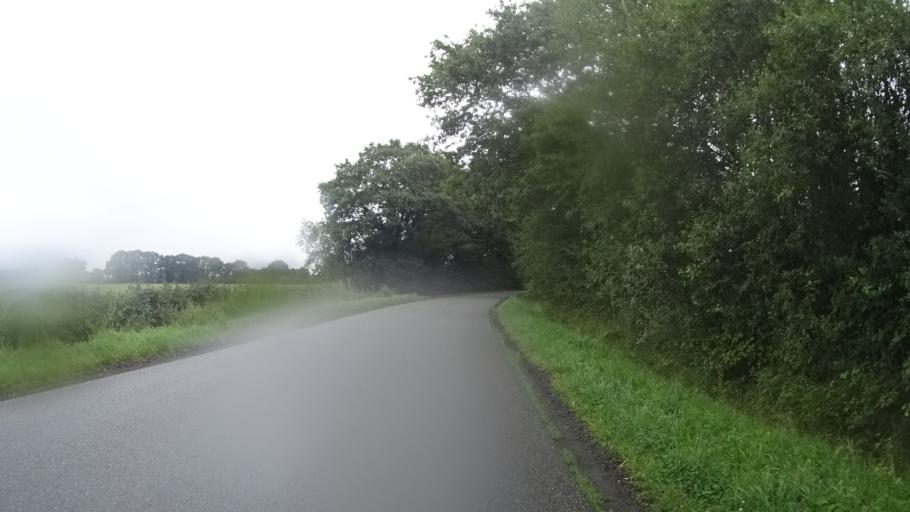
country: DE
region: Schleswig-Holstein
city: Bilsen
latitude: 53.7782
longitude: 9.8874
